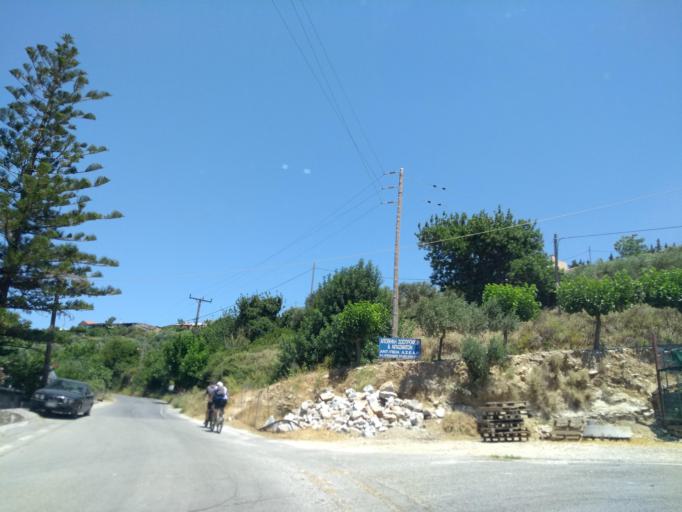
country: GR
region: Crete
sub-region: Nomos Chanias
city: Georgioupolis
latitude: 35.3256
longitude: 24.3328
